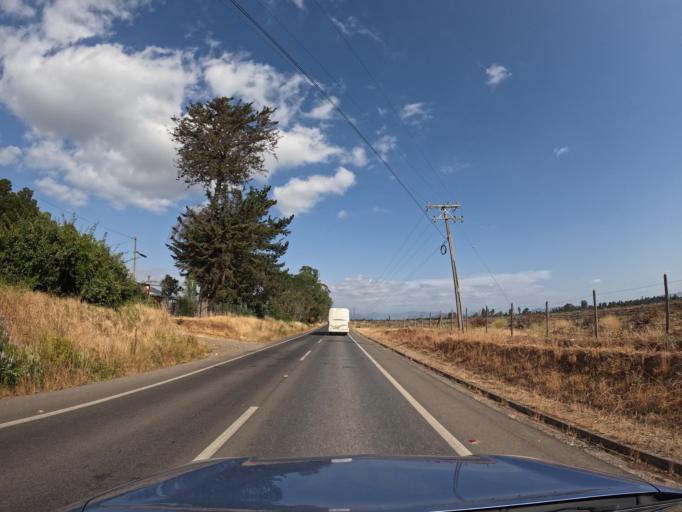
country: CL
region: Maule
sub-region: Provincia de Curico
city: Molina
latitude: -35.2670
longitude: -71.3158
